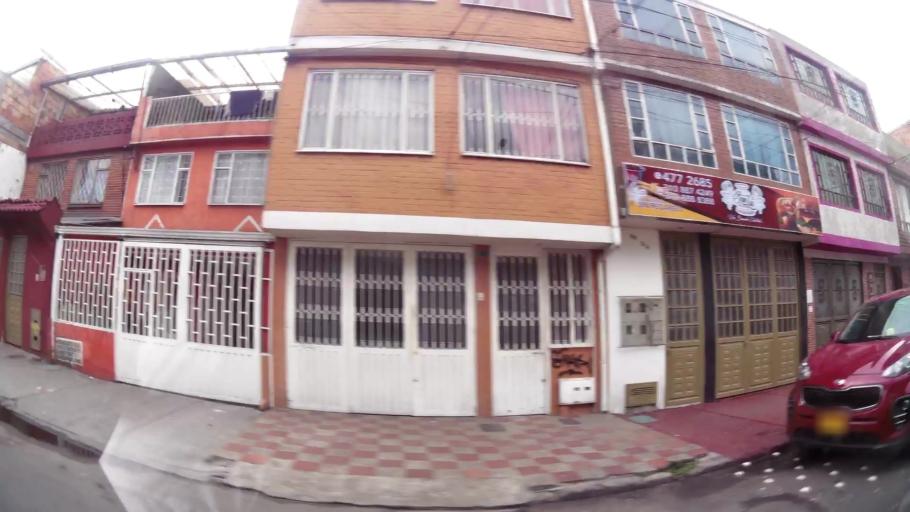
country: CO
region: Bogota D.C.
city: Bogota
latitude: 4.6775
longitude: -74.0912
